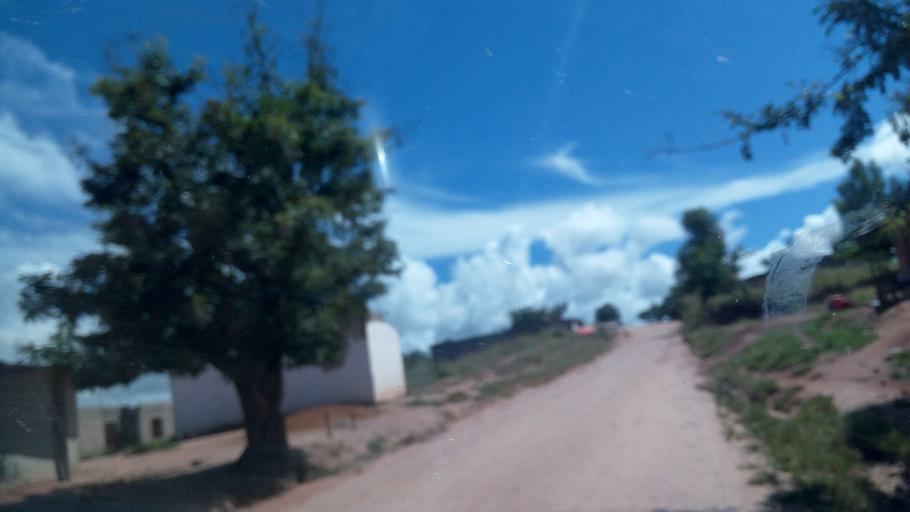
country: CD
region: Katanga
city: Kalemie
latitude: -5.8905
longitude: 29.1981
